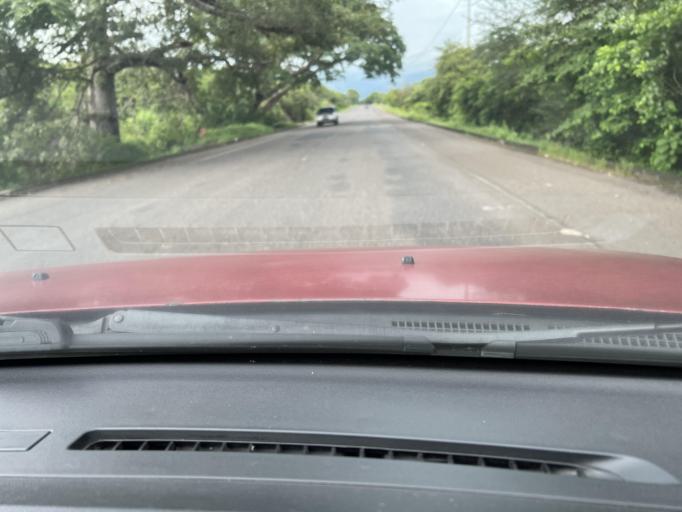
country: SV
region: La Union
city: San Alejo
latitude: 13.3999
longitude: -87.8974
